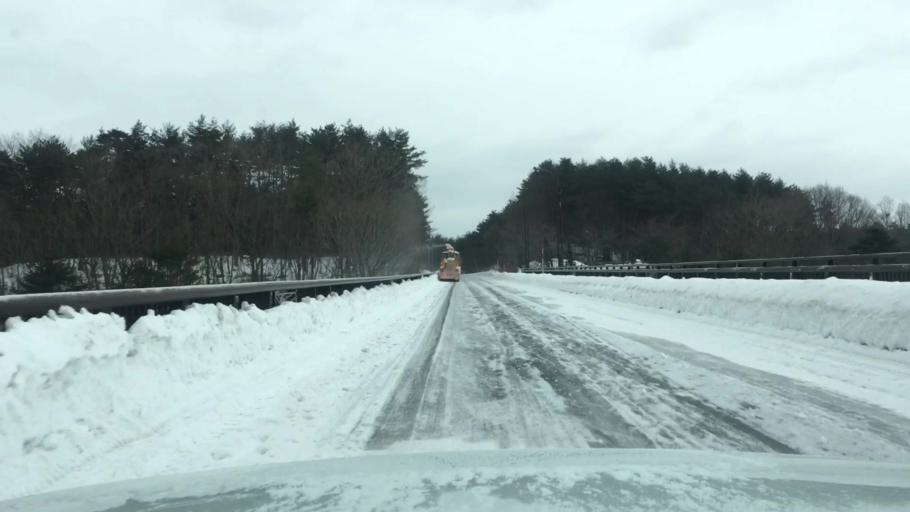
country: JP
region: Iwate
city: Shizukuishi
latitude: 39.9451
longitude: 140.9972
